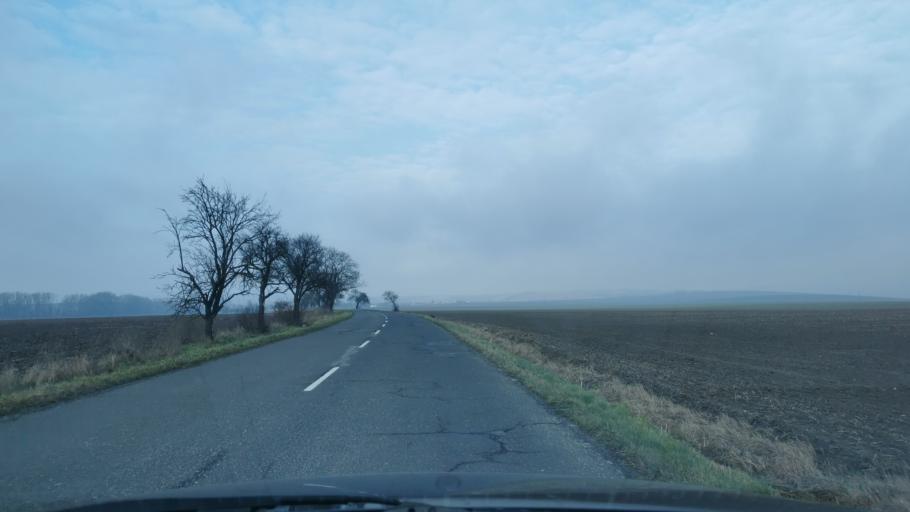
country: SK
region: Trnavsky
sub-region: Okres Senica
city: Senica
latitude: 48.6928
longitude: 17.3556
